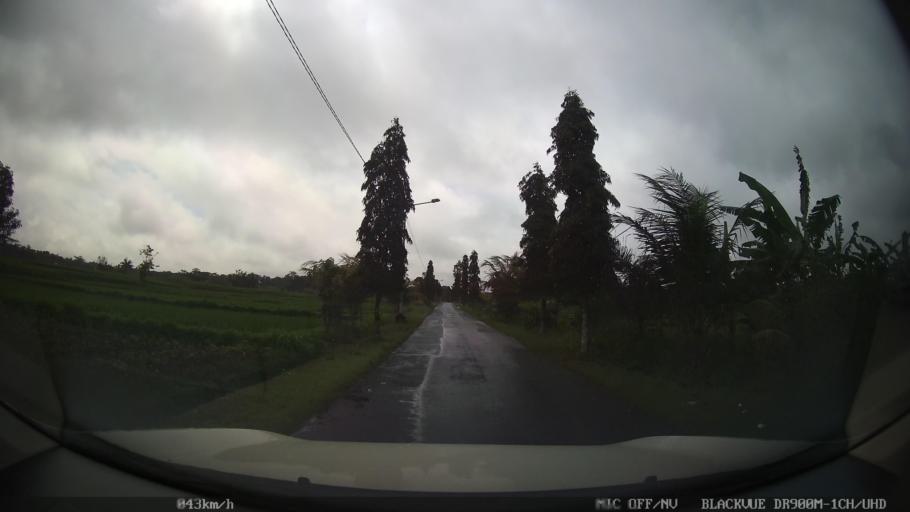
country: ID
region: Bali
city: Banjar Teguan
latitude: -8.4965
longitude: 115.2258
